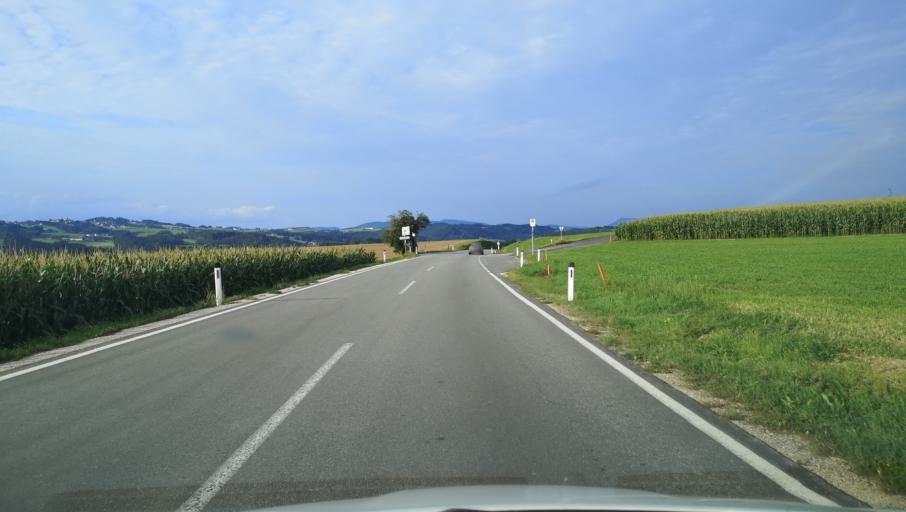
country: AT
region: Lower Austria
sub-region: Politischer Bezirk Amstetten
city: Amstetten
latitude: 48.1548
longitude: 14.9015
